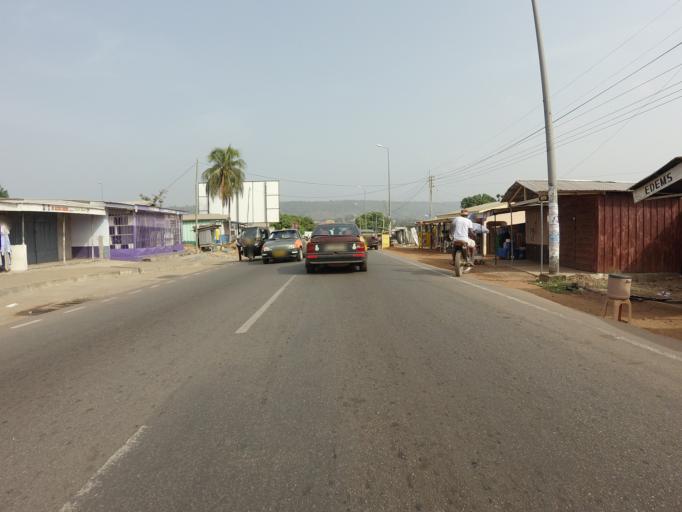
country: GH
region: Volta
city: Ho
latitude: 6.6087
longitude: 0.4749
